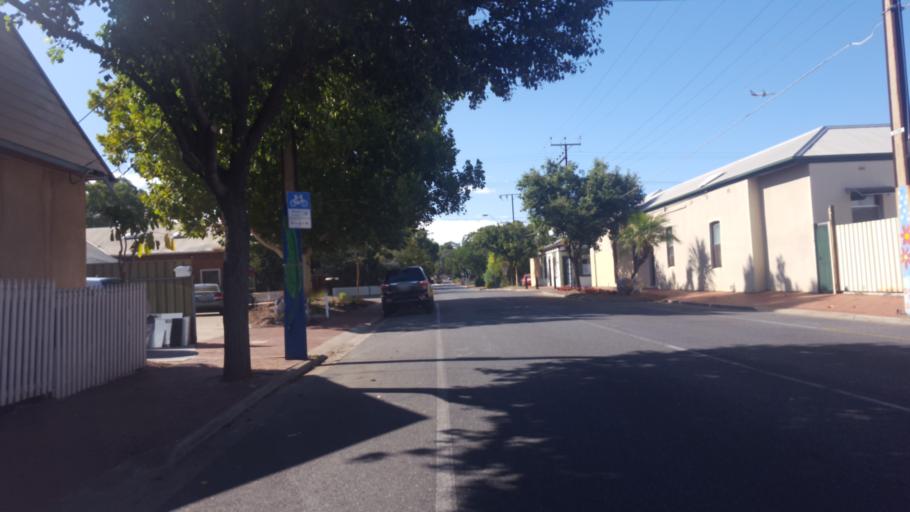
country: AU
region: South Australia
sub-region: Adelaide
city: North Adelaide
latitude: -34.9008
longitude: 138.5813
